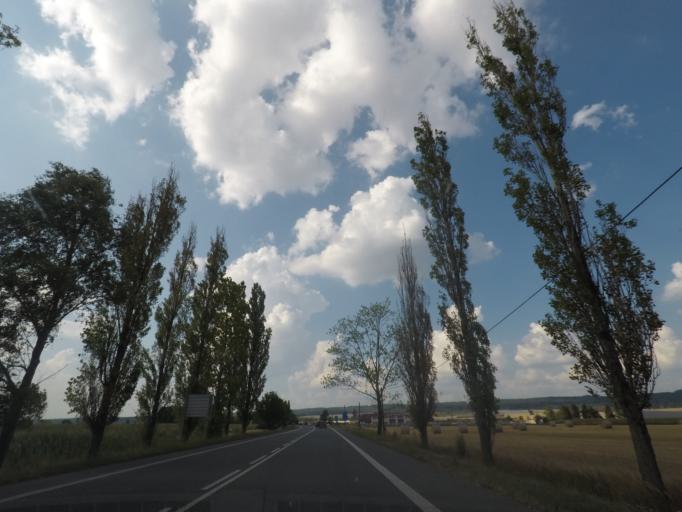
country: CZ
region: Kralovehradecky
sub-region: Okres Nachod
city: Jaromer
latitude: 50.4156
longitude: 15.8842
